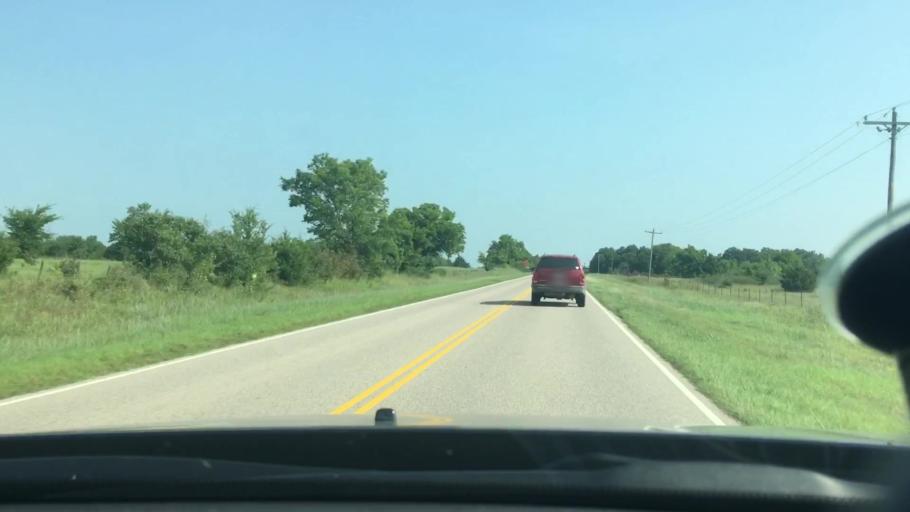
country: US
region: Oklahoma
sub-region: Johnston County
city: Tishomingo
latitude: 34.3809
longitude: -96.6359
